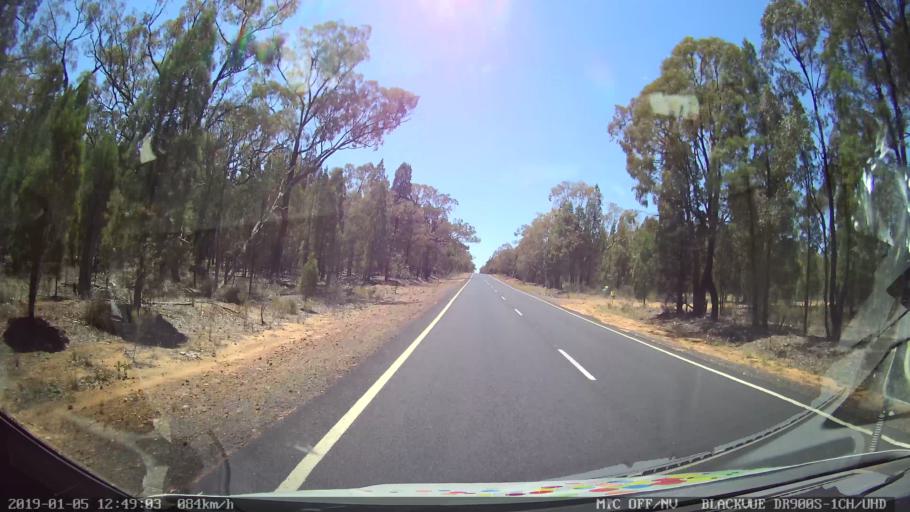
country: AU
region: New South Wales
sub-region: Warrumbungle Shire
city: Coonabarabran
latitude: -31.1178
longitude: 149.6015
